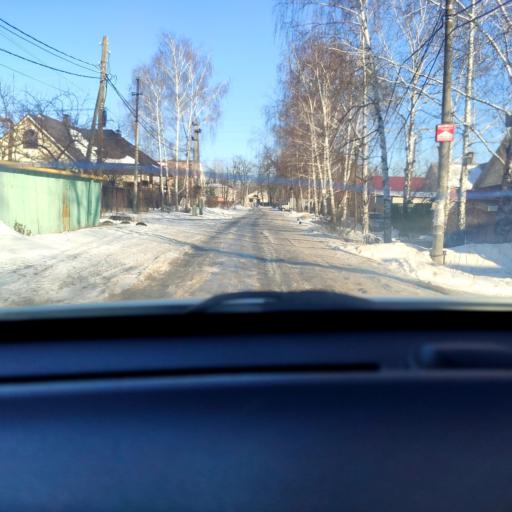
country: RU
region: Voronezj
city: Somovo
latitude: 51.7436
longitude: 39.3633
